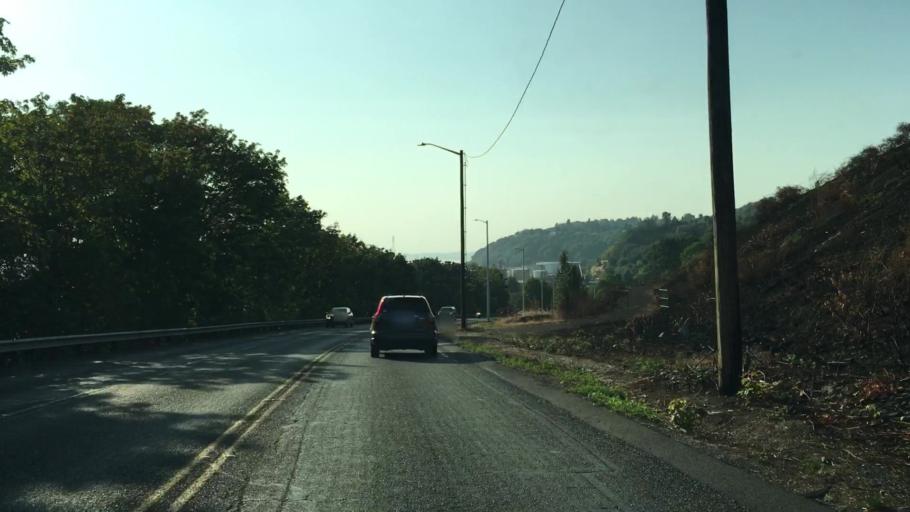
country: US
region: Washington
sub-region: Pierce County
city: Fife Heights
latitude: 47.2722
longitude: -122.3737
